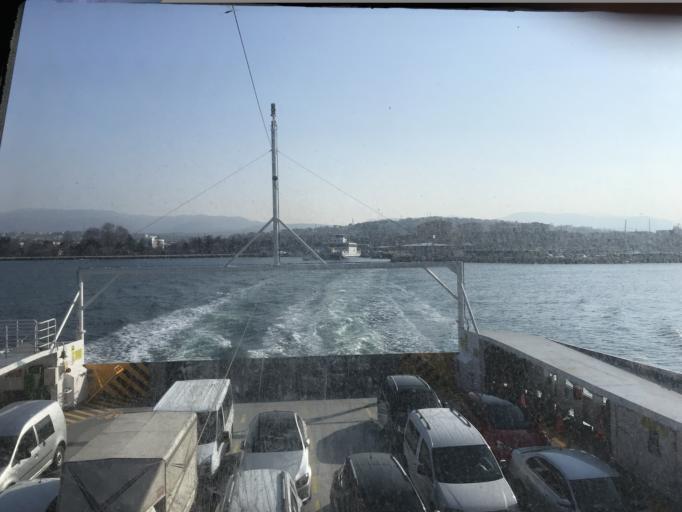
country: TR
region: Yalova
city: Yalova
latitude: 40.6645
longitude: 29.2788
